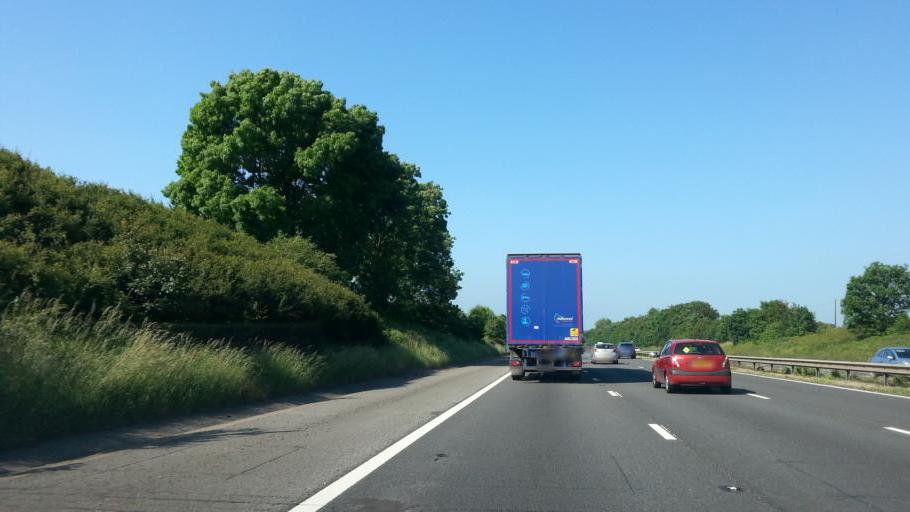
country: GB
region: England
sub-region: South Gloucestershire
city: Alveston
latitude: 51.5773
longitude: -2.5147
